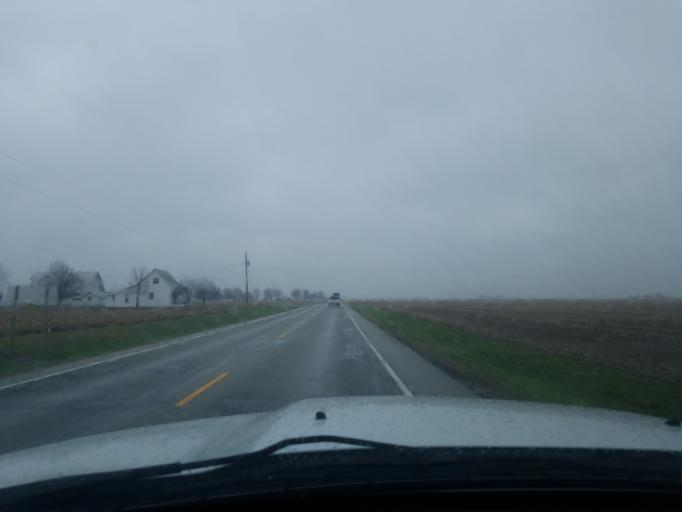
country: US
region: Indiana
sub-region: Grant County
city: Gas City
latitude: 40.4234
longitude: -85.5719
